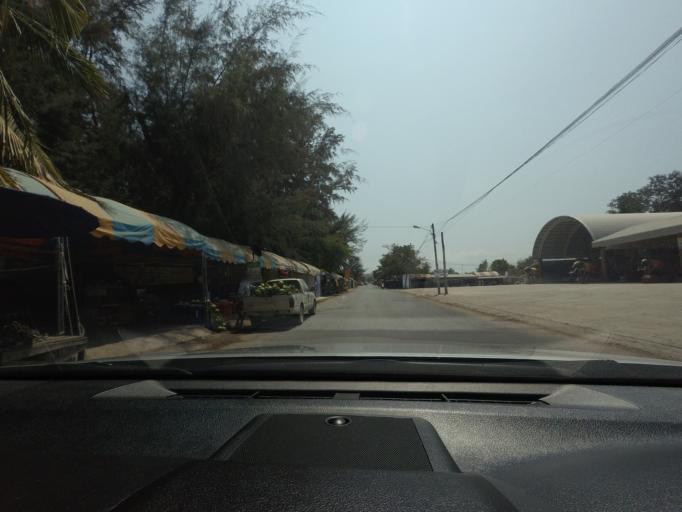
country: TH
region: Phetchaburi
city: Cha-am
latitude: 12.8130
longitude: 99.9918
